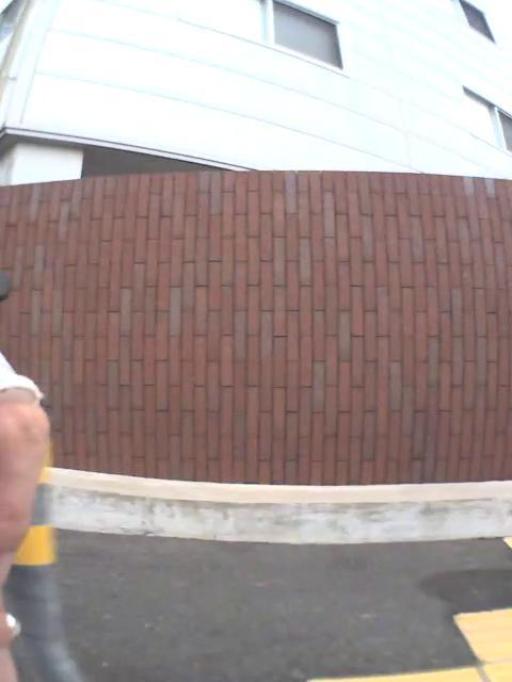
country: JP
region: Osaka
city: Neyagawa
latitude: 34.7476
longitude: 135.6231
